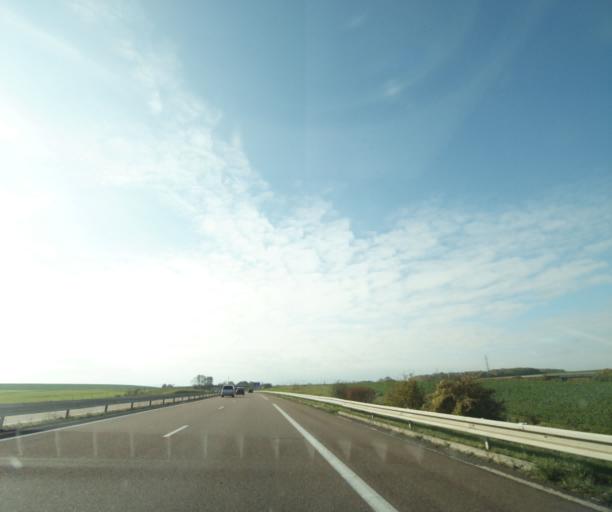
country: FR
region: Champagne-Ardenne
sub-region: Departement de la Marne
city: Jonchery-sur-Vesle
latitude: 49.2037
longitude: 3.7652
